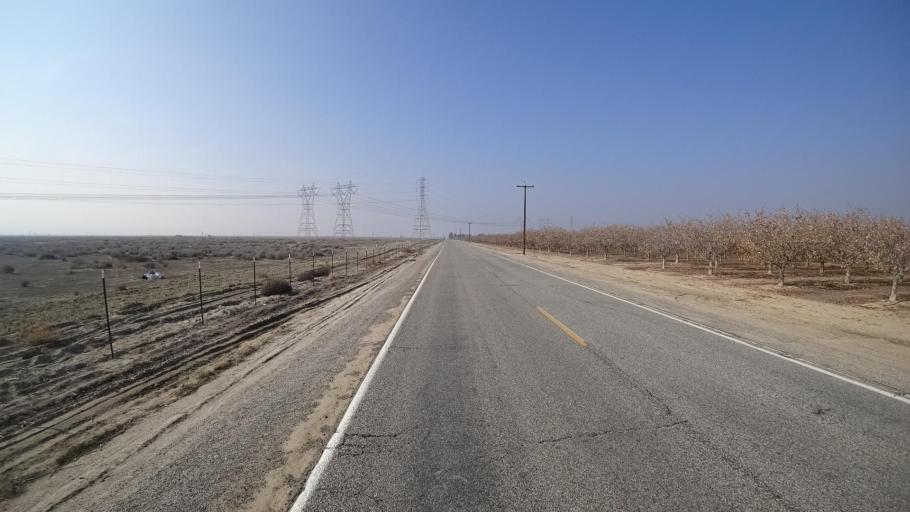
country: US
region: California
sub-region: Kern County
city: Buttonwillow
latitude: 35.3549
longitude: -119.3531
